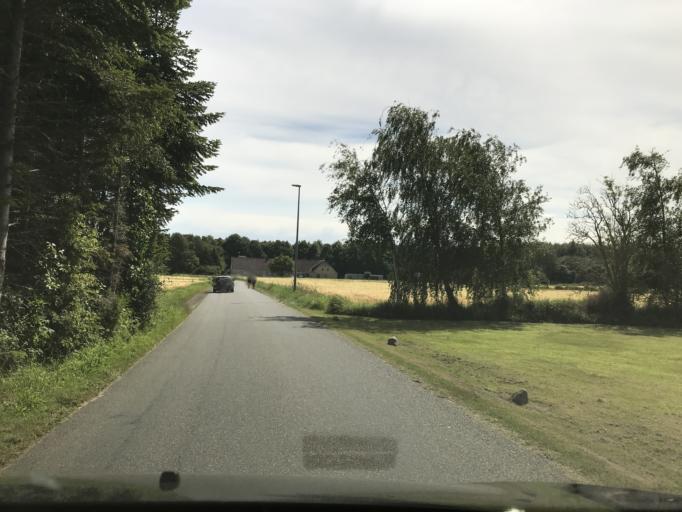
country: DK
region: South Denmark
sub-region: AEro Kommune
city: Marstal
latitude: 54.8495
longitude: 10.5108
